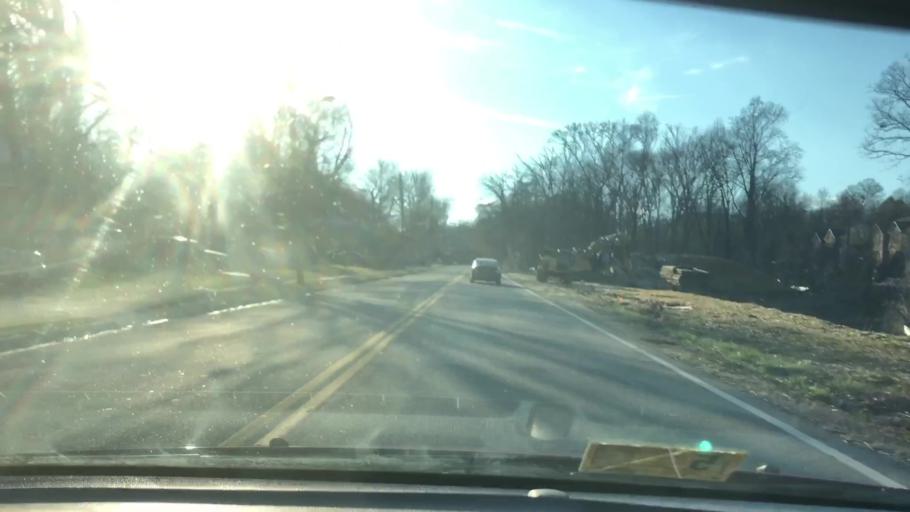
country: US
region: Virginia
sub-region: Fairfax County
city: Rose Hill
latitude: 38.7837
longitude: -77.0997
